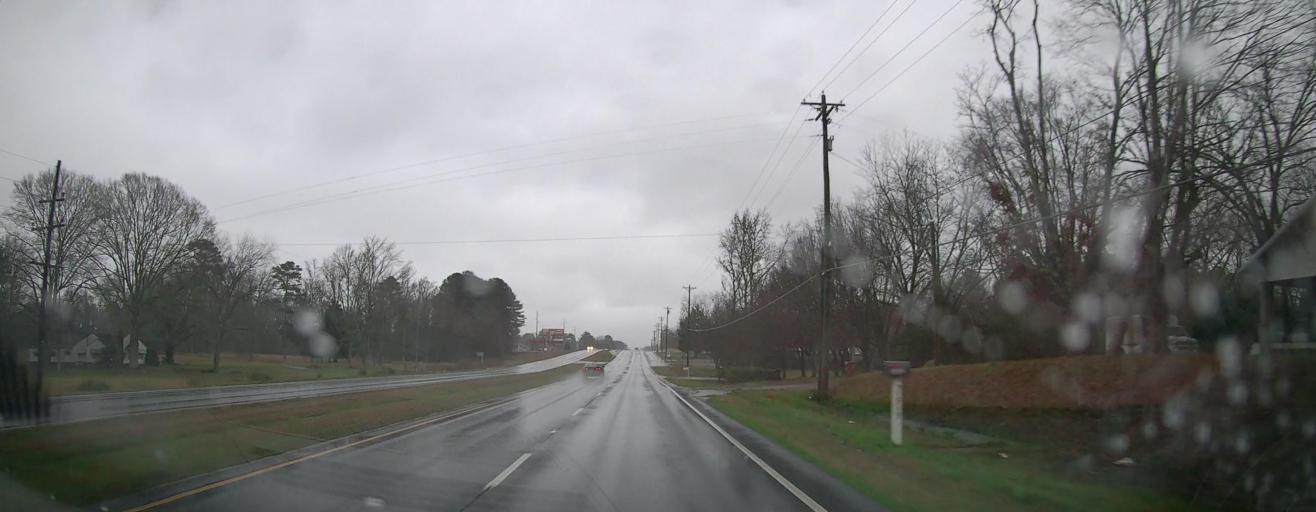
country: US
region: Alabama
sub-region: Morgan County
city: Hartselle
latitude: 34.4660
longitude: -86.9530
